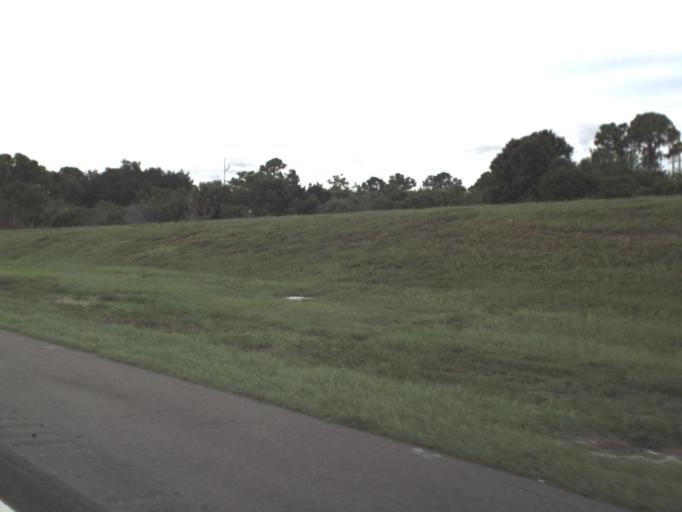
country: US
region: Florida
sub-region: Sarasota County
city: Nokomis
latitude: 27.1362
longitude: -82.4095
